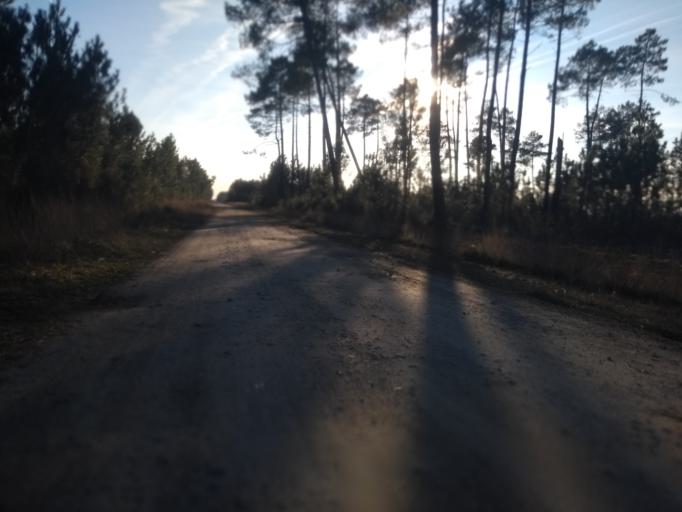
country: FR
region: Aquitaine
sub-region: Departement de la Gironde
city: Le Barp
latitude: 44.5977
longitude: -0.8001
